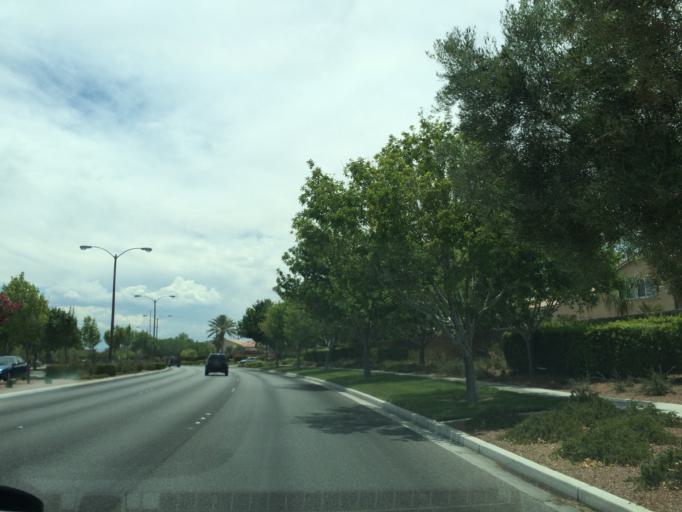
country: US
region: Nevada
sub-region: Clark County
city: North Las Vegas
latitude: 36.2799
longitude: -115.1790
